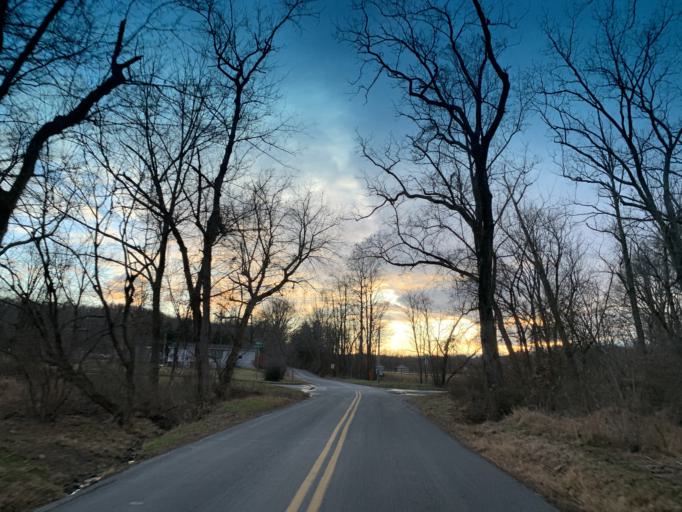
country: US
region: Maryland
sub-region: Harford County
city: Bel Air North
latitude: 39.6150
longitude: -76.3153
